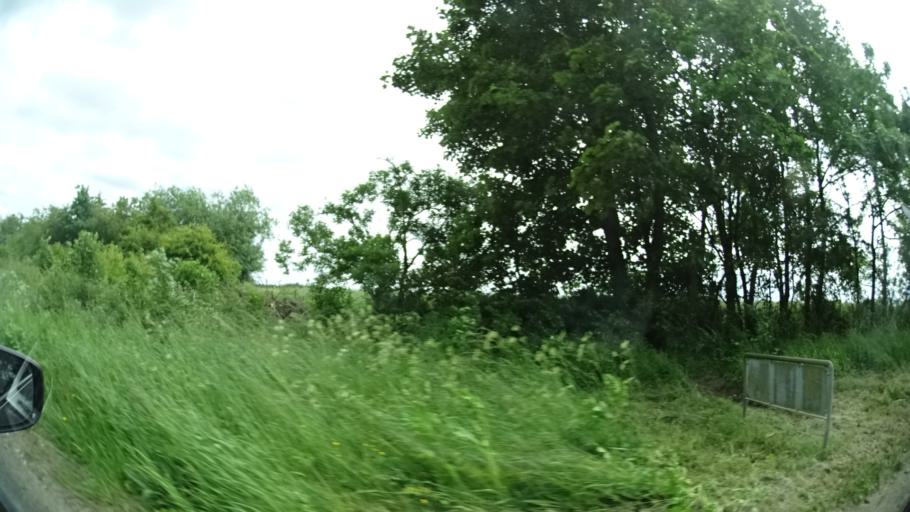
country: DK
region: Central Jutland
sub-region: Syddjurs Kommune
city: Ryomgard
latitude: 56.4274
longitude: 10.6122
